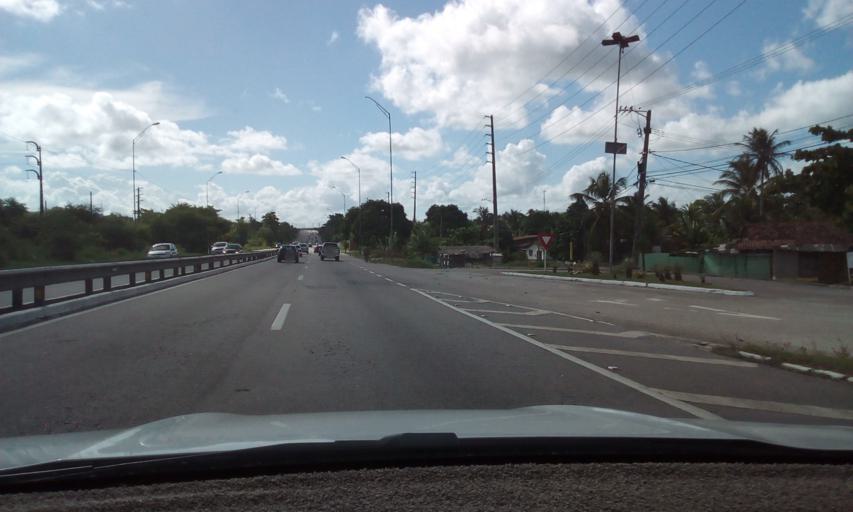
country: BR
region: Paraiba
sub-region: Bayeux
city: Bayeux
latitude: -7.1396
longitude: -34.9228
